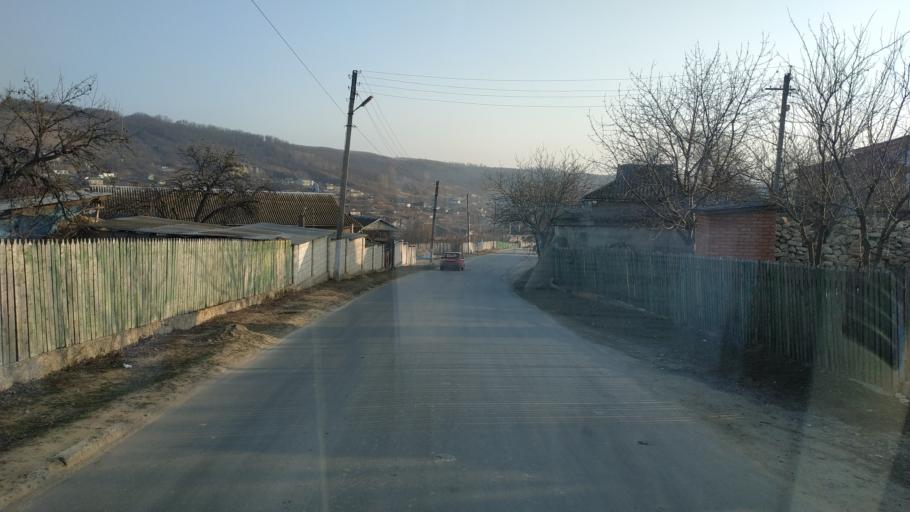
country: MD
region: Hincesti
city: Dancu
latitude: 46.7667
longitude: 28.3594
